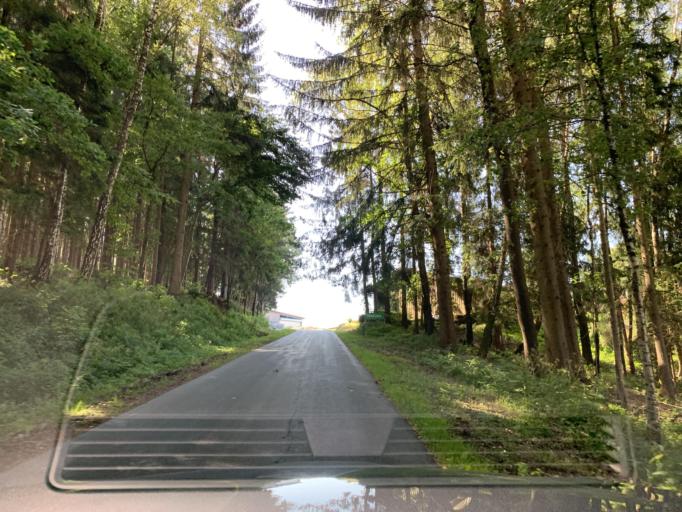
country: DE
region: Bavaria
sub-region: Upper Palatinate
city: Dieterskirchen
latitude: 49.4103
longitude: 12.4346
